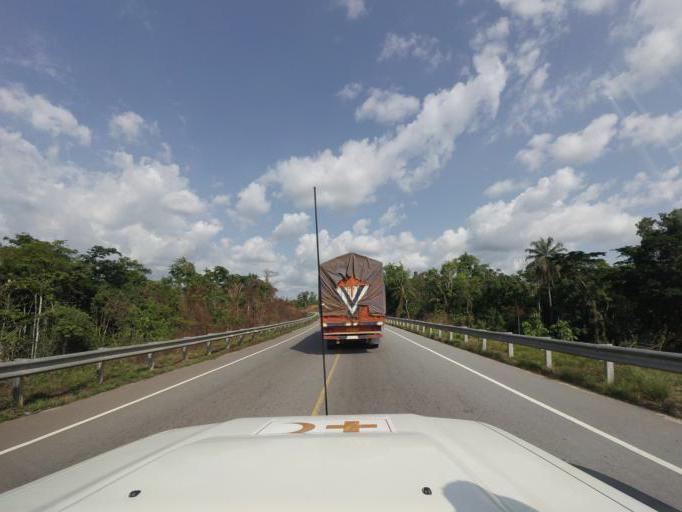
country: LR
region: Bong
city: Gbarnga
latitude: 6.8792
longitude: -9.7273
